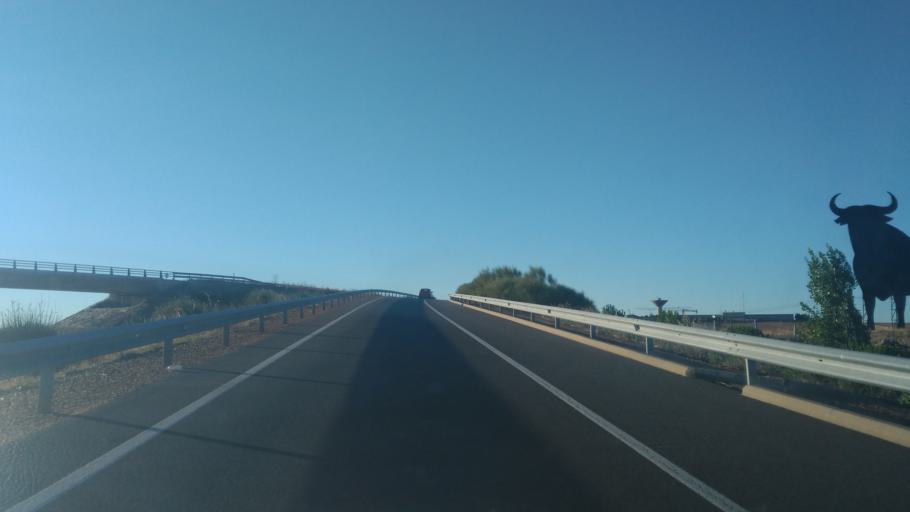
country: ES
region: Castille and Leon
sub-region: Provincia de Salamanca
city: Carbajosa de la Sagrada
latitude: 40.9223
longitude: -5.6674
